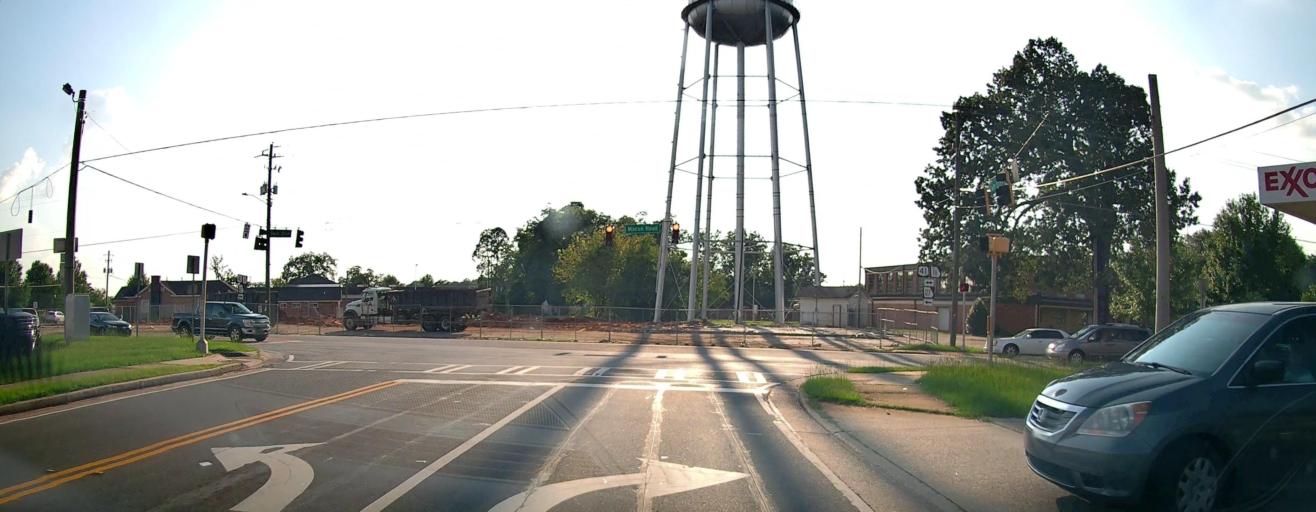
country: US
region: Georgia
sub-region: Houston County
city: Perry
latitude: 32.4606
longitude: -83.7304
